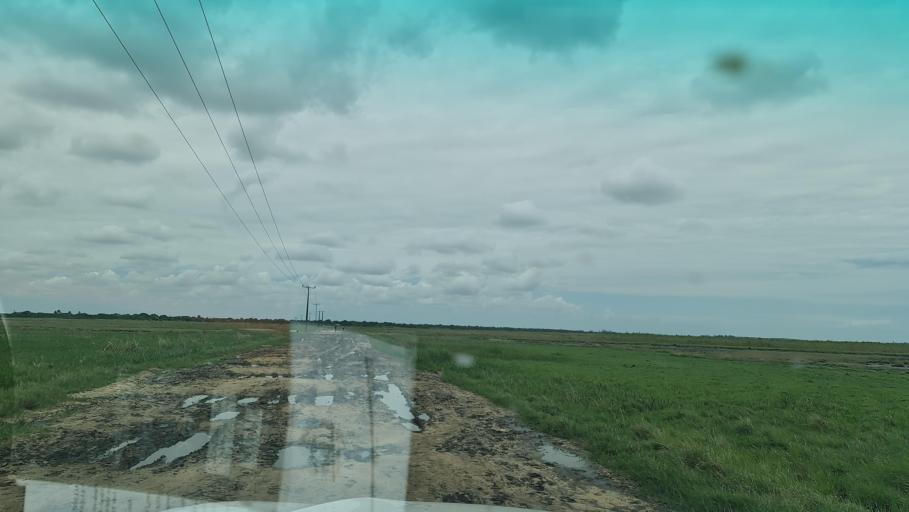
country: MZ
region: Maputo City
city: Maputo
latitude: -25.7141
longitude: 32.7025
